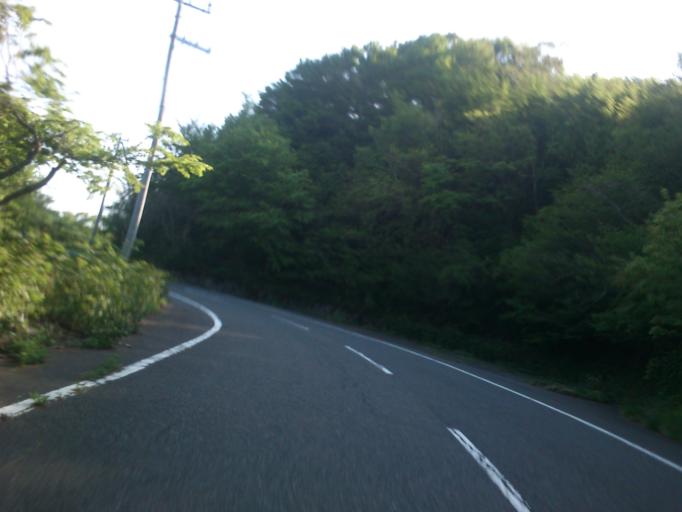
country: JP
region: Kyoto
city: Miyazu
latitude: 35.7234
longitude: 135.1876
